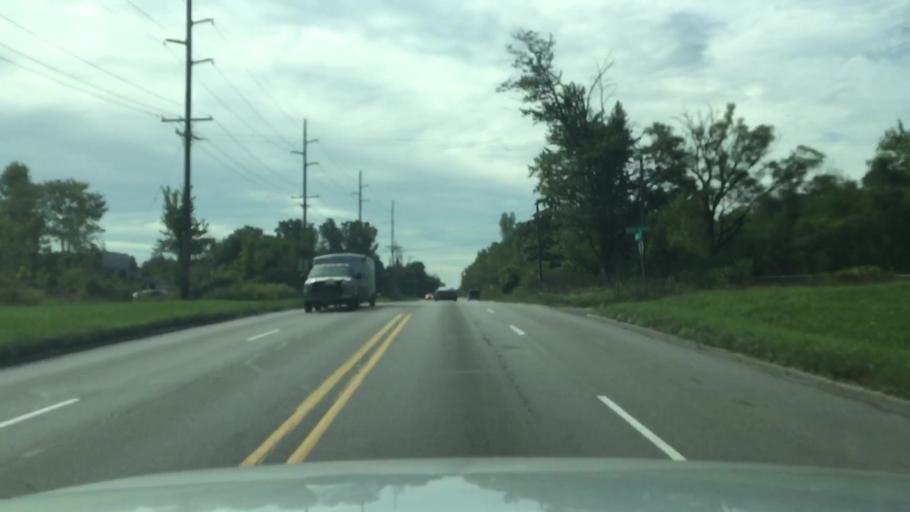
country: US
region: Michigan
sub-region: Wayne County
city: Canton
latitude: 42.2602
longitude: -83.4868
